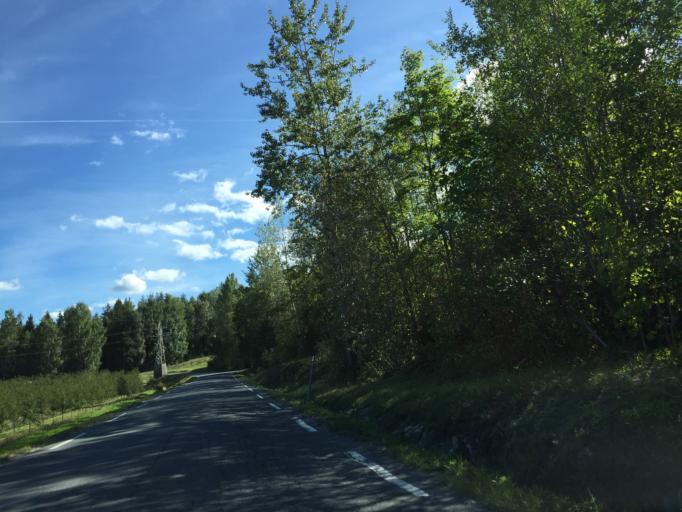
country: NO
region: Buskerud
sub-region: Ovre Eiker
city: Hokksund
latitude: 59.6956
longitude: 9.8405
